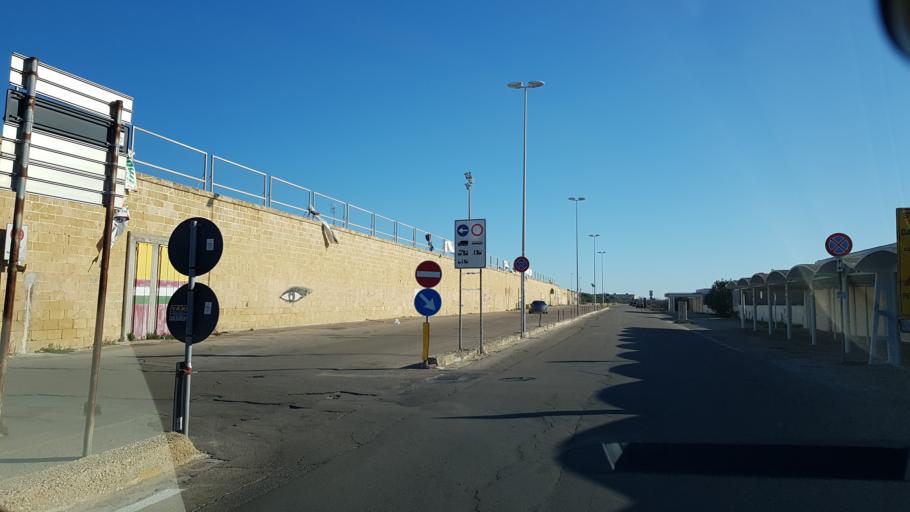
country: IT
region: Apulia
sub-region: Provincia di Lecce
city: Gallipoli
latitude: 40.0468
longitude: 18.0059
